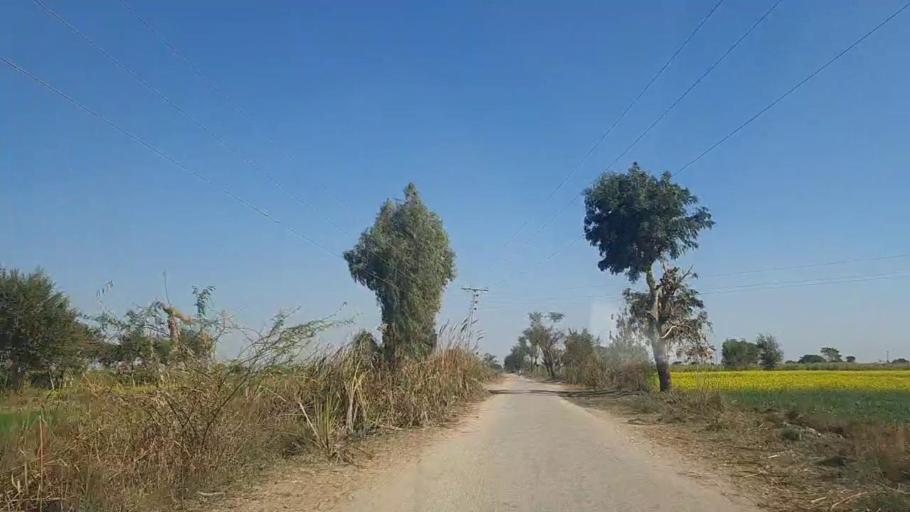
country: PK
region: Sindh
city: Sanghar
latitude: 26.2208
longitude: 68.9321
